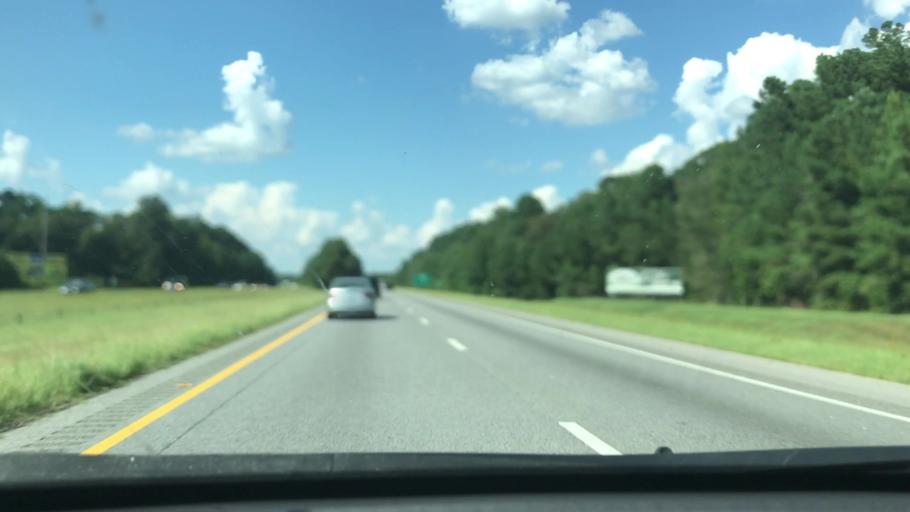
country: US
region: South Carolina
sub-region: Orangeburg County
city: Holly Hill
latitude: 33.4396
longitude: -80.4836
